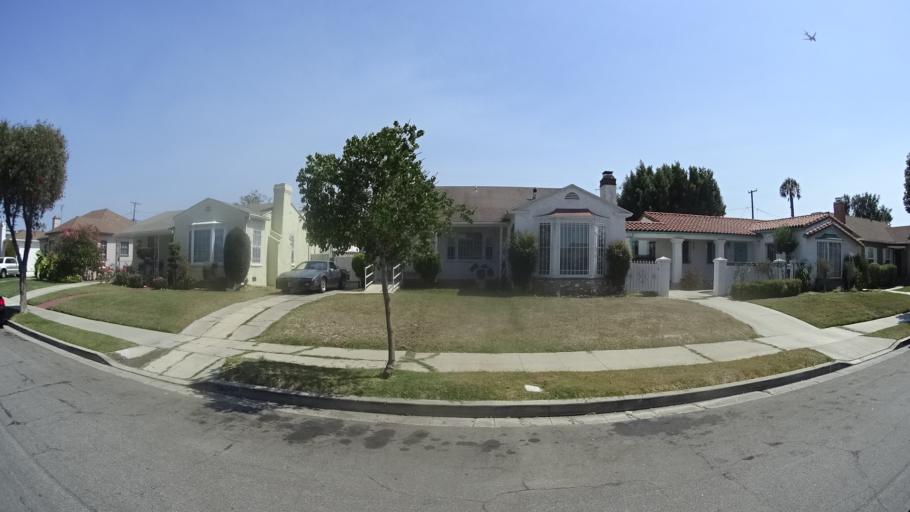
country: US
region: California
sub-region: Los Angeles County
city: Inglewood
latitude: 33.9632
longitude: -118.3234
